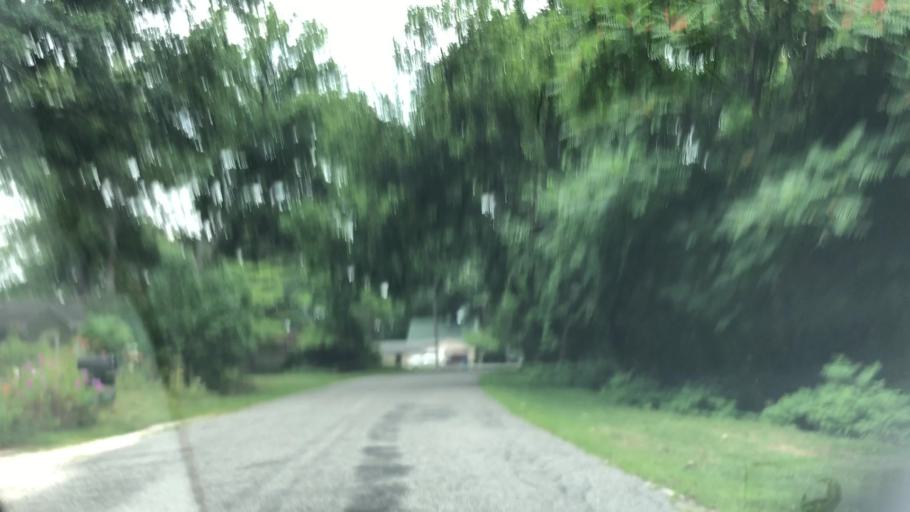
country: US
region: Ohio
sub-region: Summit County
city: Portage Lakes
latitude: 41.0093
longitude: -81.5390
